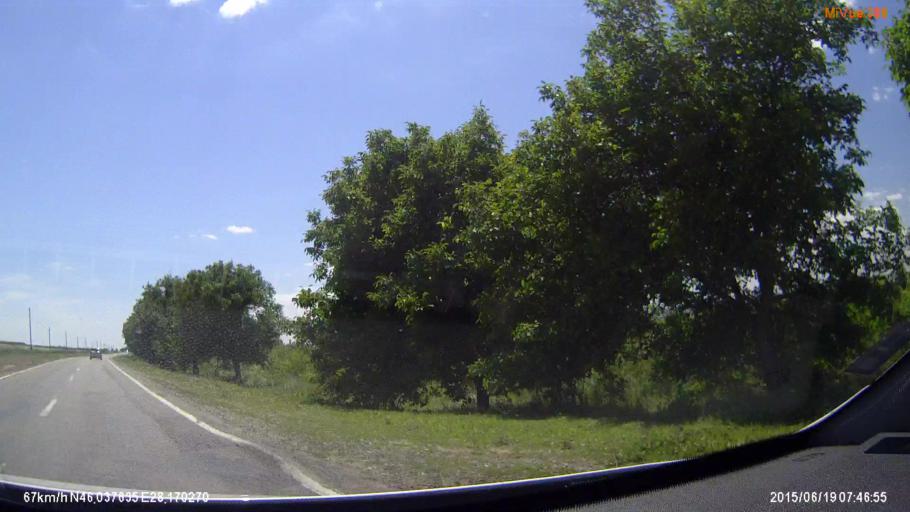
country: RO
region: Vaslui
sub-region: Oras Murgeni
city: Carja
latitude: 46.0381
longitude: 28.1703
